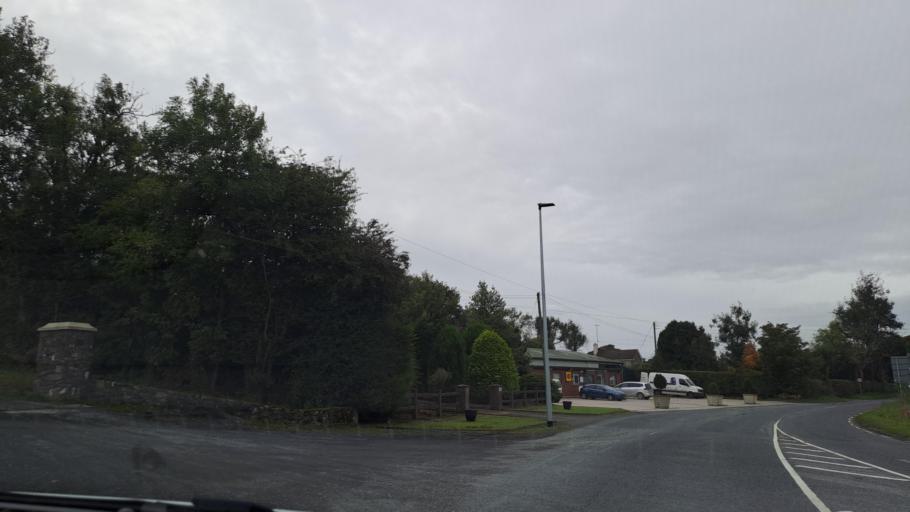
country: IE
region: Ulster
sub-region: County Monaghan
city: Castleblayney
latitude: 54.0652
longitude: -6.8134
